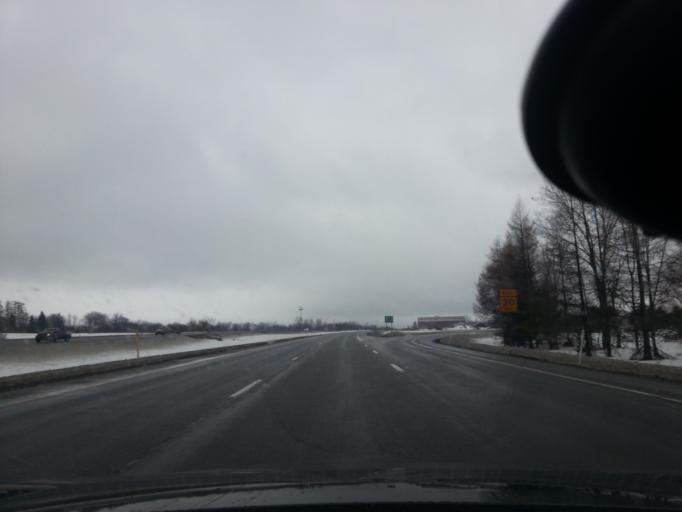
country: US
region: New York
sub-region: Jefferson County
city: Adams
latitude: 43.8175
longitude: -76.0325
